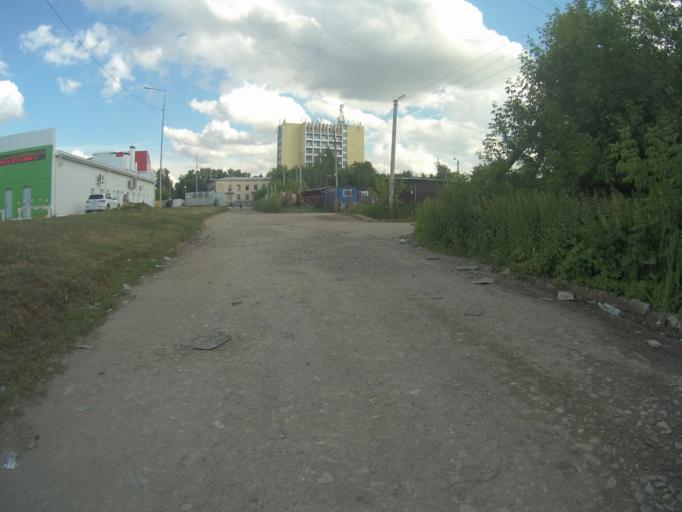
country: RU
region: Vladimir
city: Bogolyubovo
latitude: 56.1747
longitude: 40.4904
